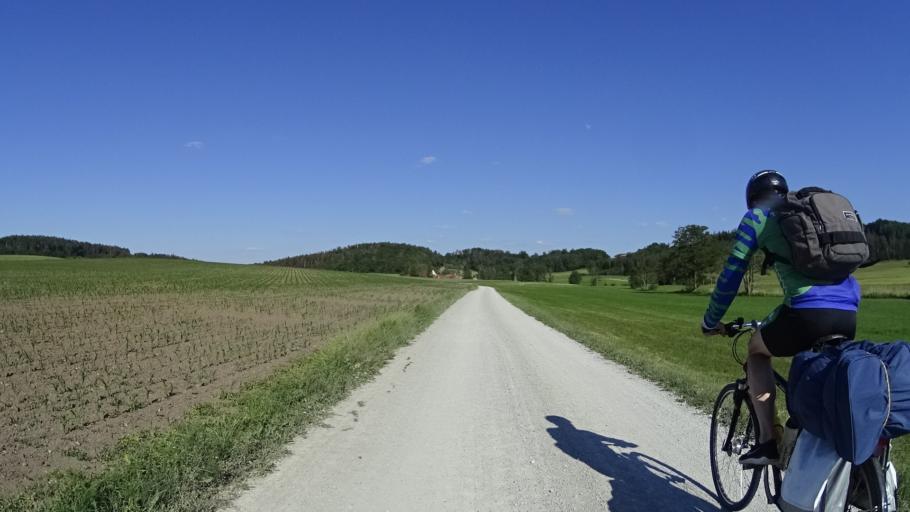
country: DE
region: Bavaria
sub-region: Regierungsbezirk Mittelfranken
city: Feuchtwangen
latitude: 49.2030
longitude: 10.3238
